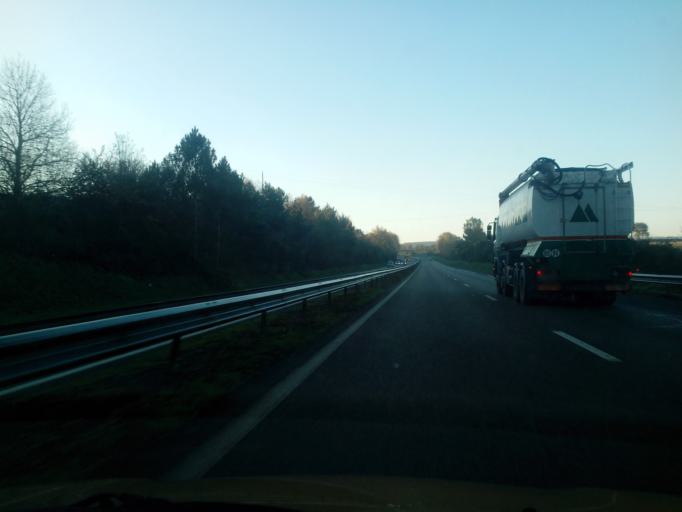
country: FR
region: Brittany
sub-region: Departement du Morbihan
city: Malestroit
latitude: 47.8313
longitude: -2.4310
